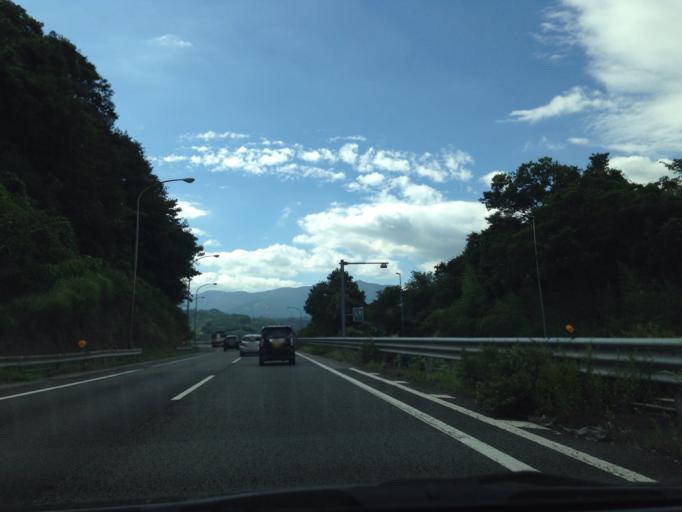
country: JP
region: Shizuoka
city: Gotemba
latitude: 35.3580
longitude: 138.9957
